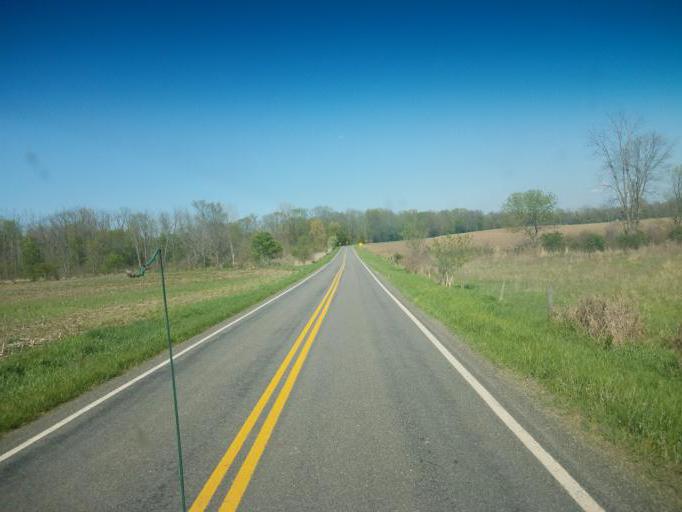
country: US
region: Ohio
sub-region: Medina County
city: Westfield Center
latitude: 40.9992
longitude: -81.9488
